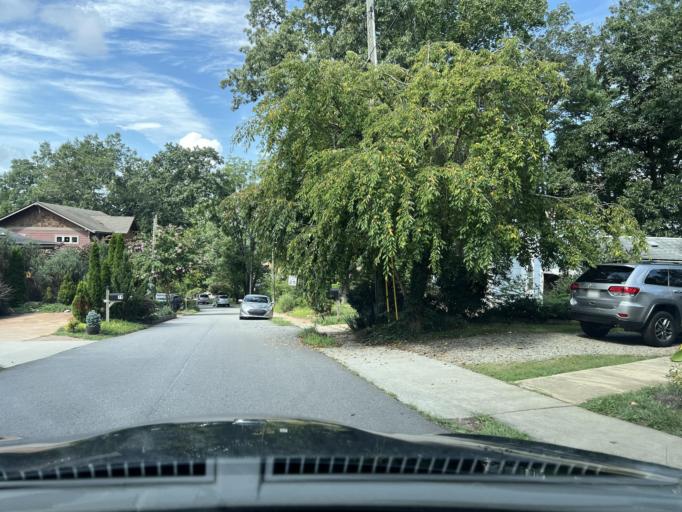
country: US
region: North Carolina
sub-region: Buncombe County
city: Asheville
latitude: 35.5716
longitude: -82.5416
